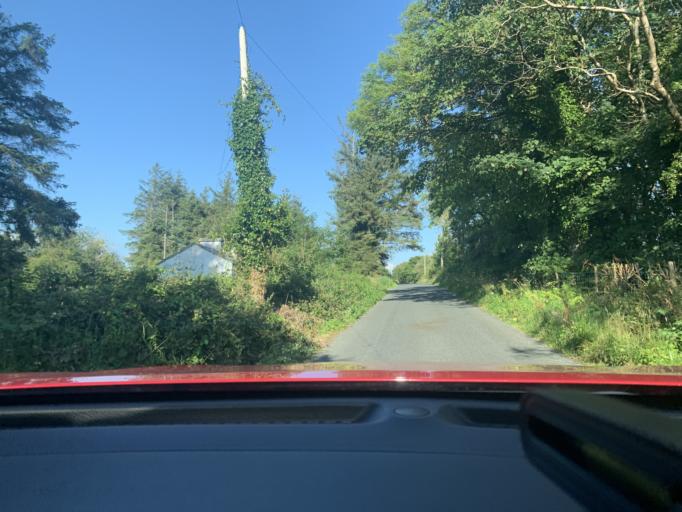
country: IE
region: Connaught
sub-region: Sligo
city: Tobercurry
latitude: 54.1339
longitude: -8.7110
